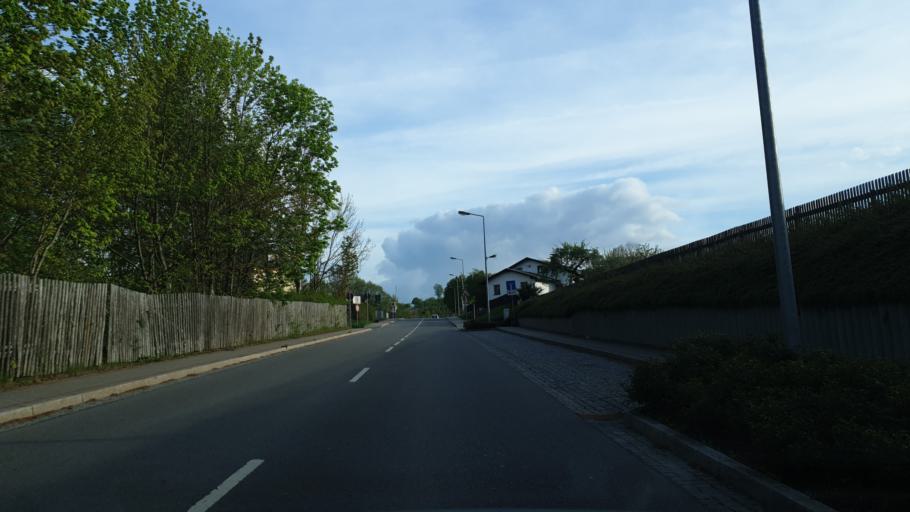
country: DE
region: Saxony
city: Lichtenstein
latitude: 50.7469
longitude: 12.6370
